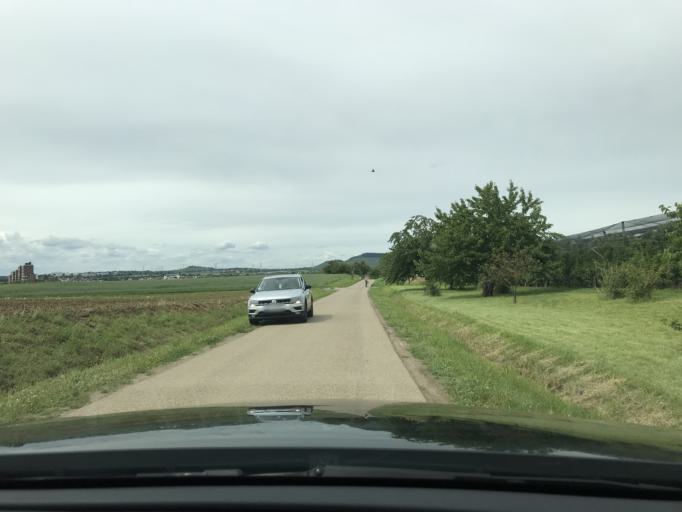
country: DE
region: Baden-Wuerttemberg
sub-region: Regierungsbezirk Stuttgart
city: Weinstadt-Endersbach
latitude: 48.8015
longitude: 9.3605
